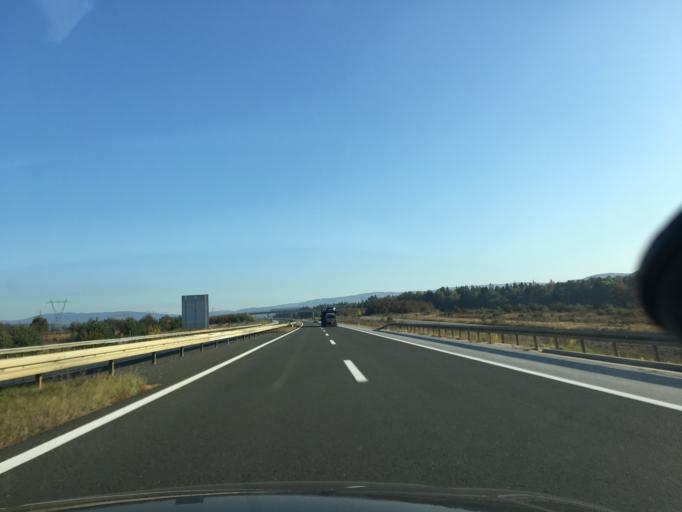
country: HR
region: Licko-Senjska
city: Gospic
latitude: 44.5859
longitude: 15.4322
